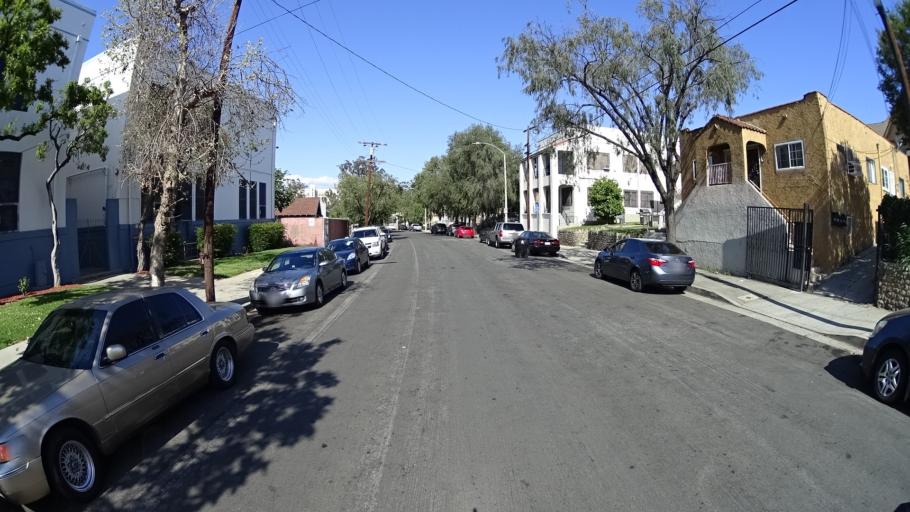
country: US
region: California
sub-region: Los Angeles County
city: Boyle Heights
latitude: 34.0525
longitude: -118.2167
